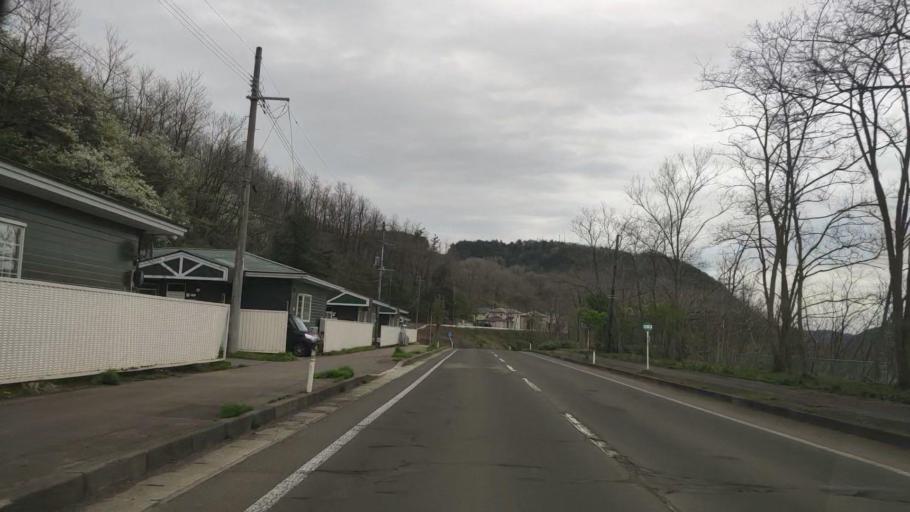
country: JP
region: Akita
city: Hanawa
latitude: 40.3277
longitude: 140.7475
